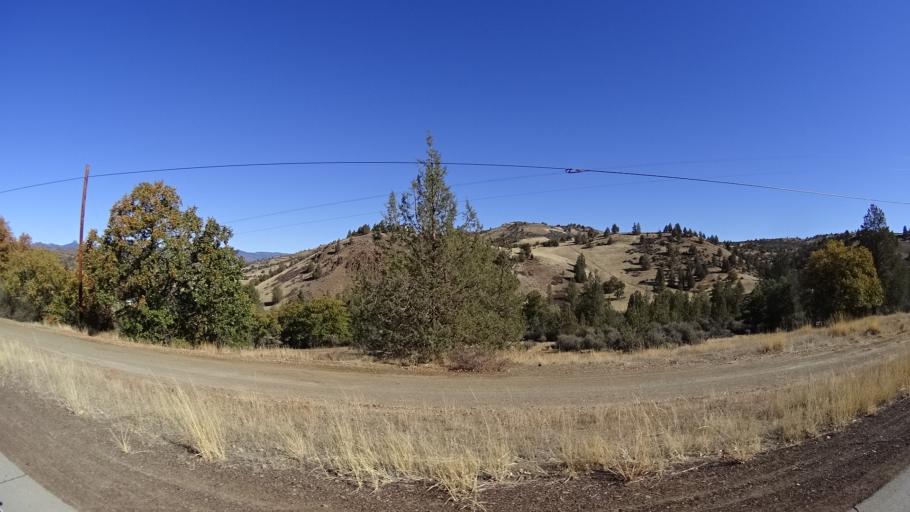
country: US
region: California
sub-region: Siskiyou County
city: Montague
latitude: 41.8725
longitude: -122.4755
